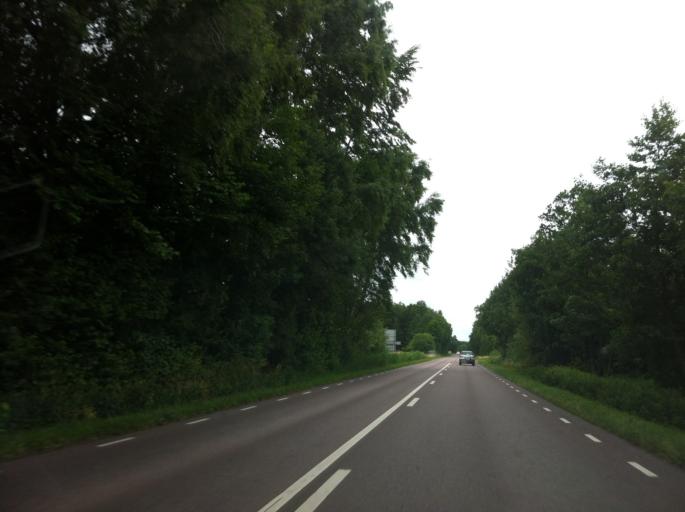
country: SE
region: Kalmar
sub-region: Borgholms Kommun
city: Borgholm
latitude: 57.1773
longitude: 17.0285
